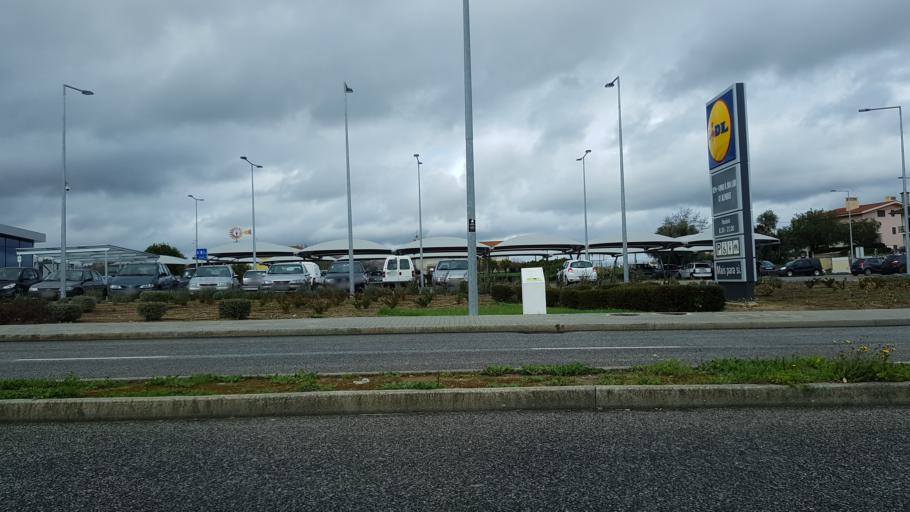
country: PT
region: Lisbon
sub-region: Alenquer
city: Carregado
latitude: 39.0403
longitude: -8.9875
